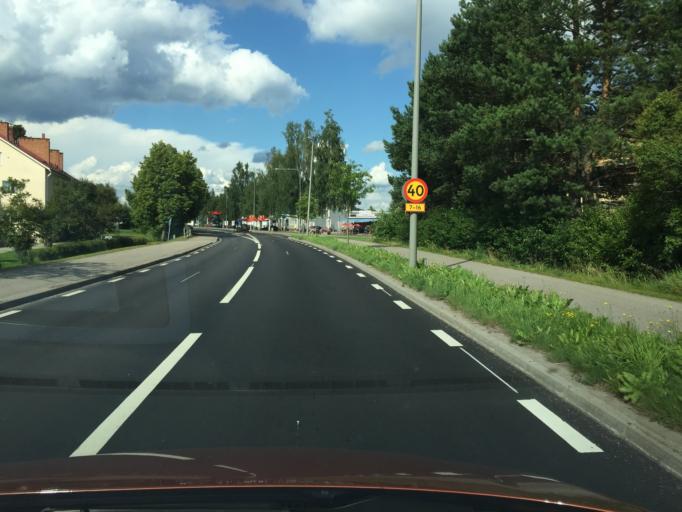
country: SE
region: Gaevleborg
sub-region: Bollnas Kommun
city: Arbra
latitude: 61.5159
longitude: 16.3630
